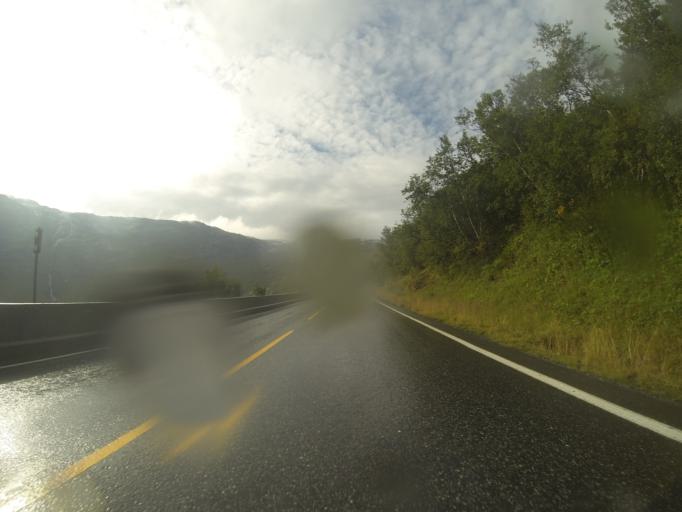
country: NO
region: Hordaland
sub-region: Odda
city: Odda
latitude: 59.8210
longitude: 6.7469
